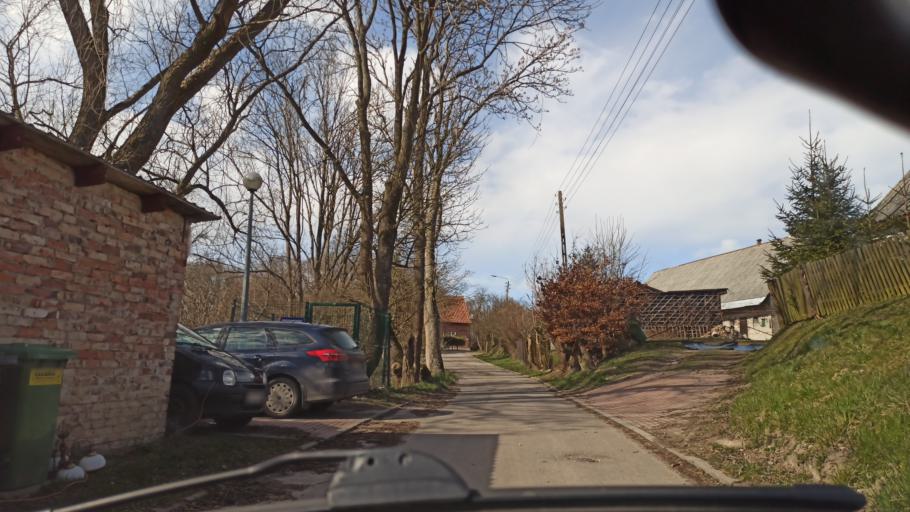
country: PL
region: Warmian-Masurian Voivodeship
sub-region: Powiat elblaski
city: Tolkmicko
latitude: 54.2701
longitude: 19.4728
